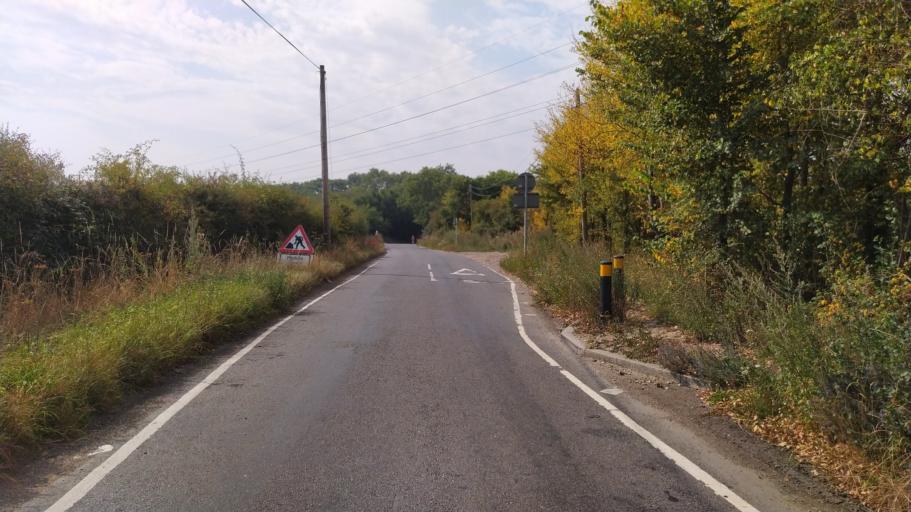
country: GB
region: England
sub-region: Hampshire
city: Romsey
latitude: 50.9874
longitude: -1.4621
